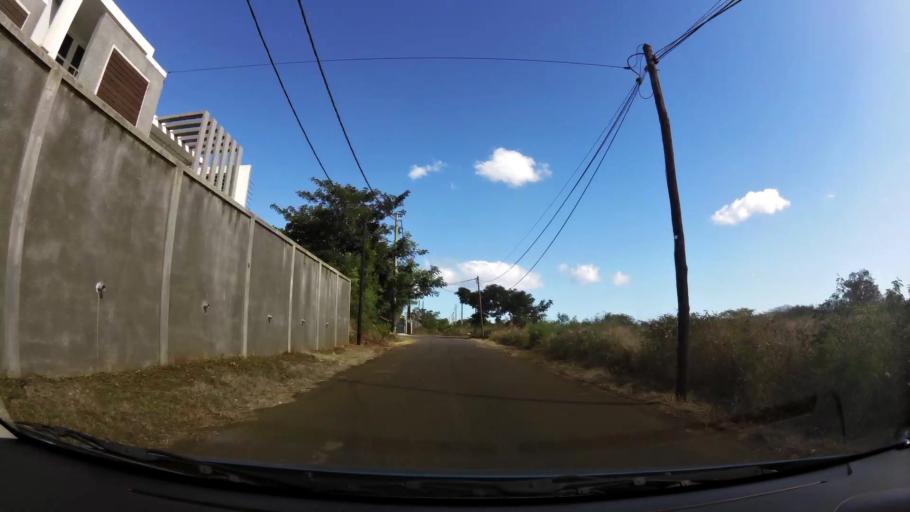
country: MU
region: Black River
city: Albion
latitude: -20.2265
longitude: 57.4148
